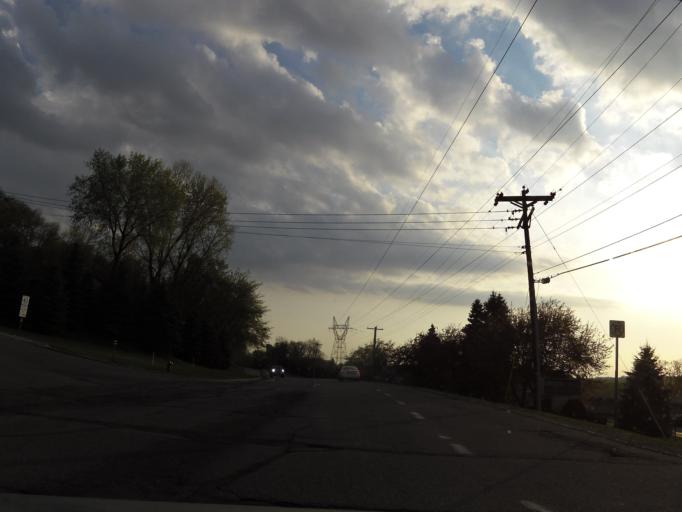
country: US
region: Minnesota
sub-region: Dakota County
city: Mendota Heights
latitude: 44.8960
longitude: -93.1466
